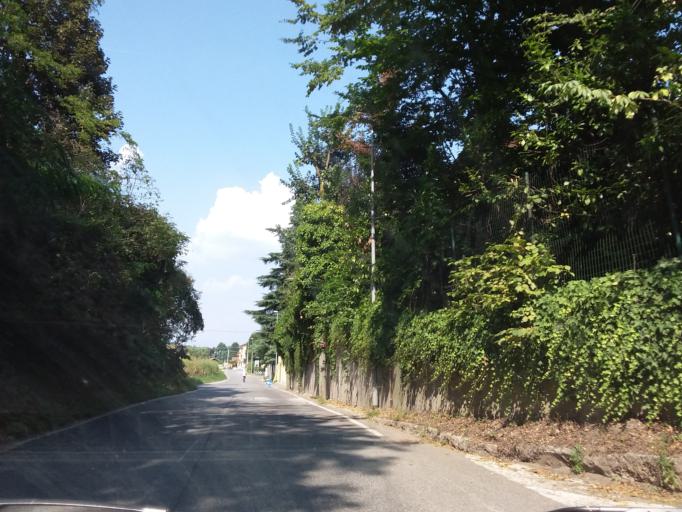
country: IT
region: Piedmont
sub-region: Provincia di Torino
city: Pianezza
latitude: 45.0848
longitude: 7.5478
